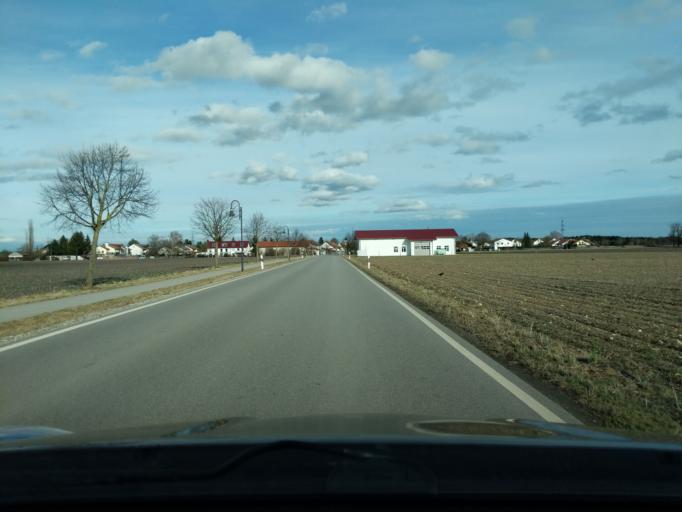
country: DE
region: Bavaria
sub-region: Upper Bavaria
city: Vaterstetten
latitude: 48.1130
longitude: 11.7894
